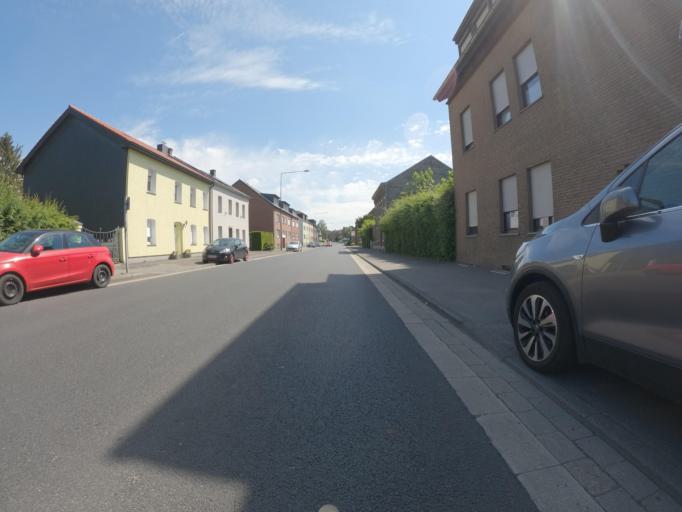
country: DE
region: North Rhine-Westphalia
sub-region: Regierungsbezirk Koln
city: Wurselen
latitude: 50.7757
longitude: 6.1688
